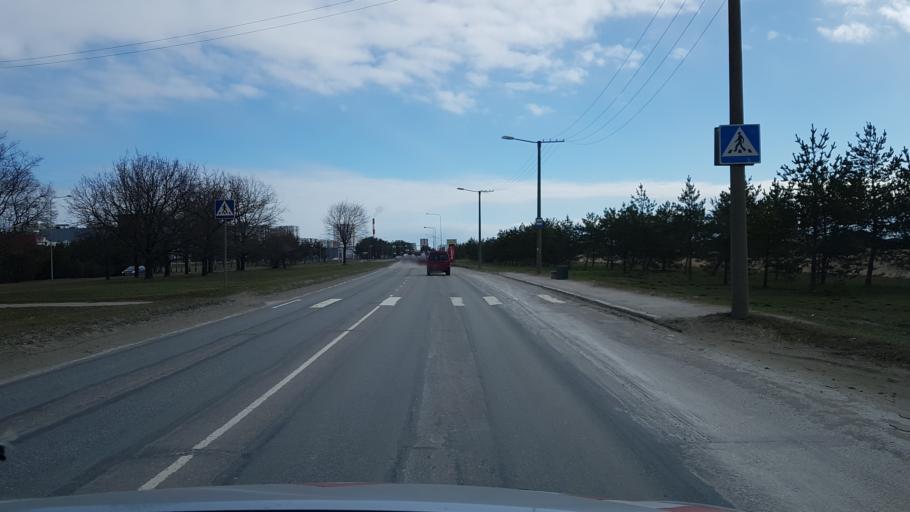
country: EE
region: Harju
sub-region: Tallinna linn
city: Kose
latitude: 59.4349
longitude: 24.8688
